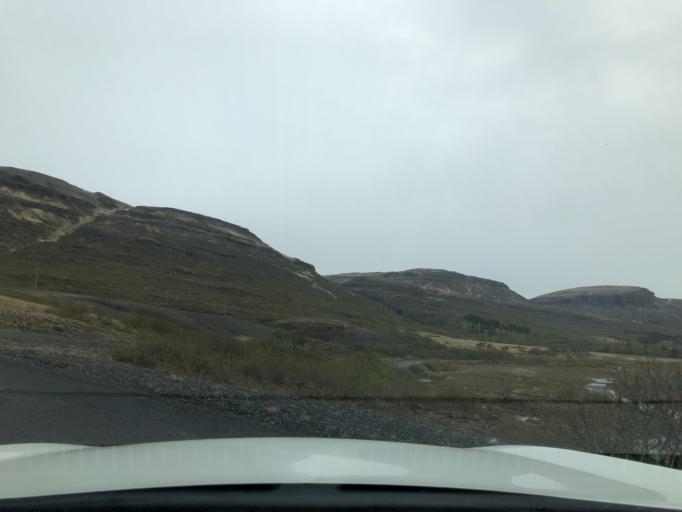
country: IS
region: South
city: Hveragerdi
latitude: 64.3844
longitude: -21.3412
